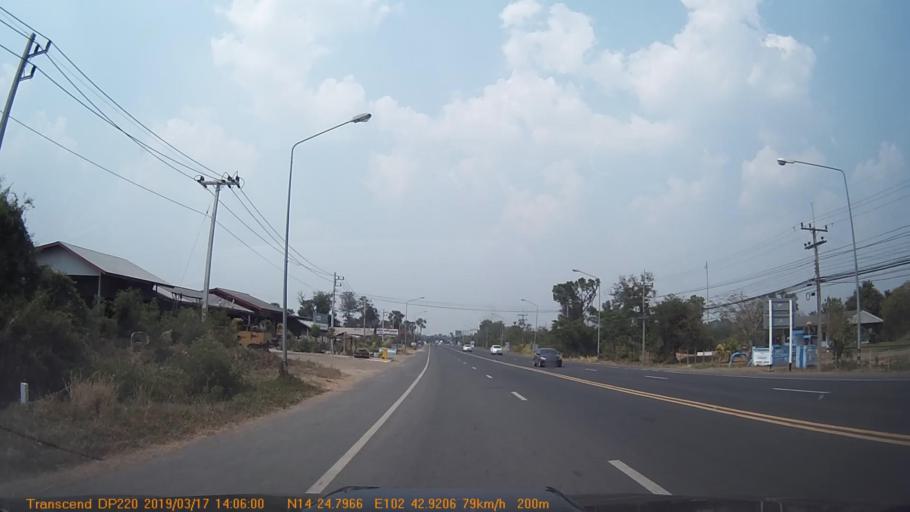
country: TH
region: Buriram
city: Pa Kham
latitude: 14.4137
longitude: 102.7154
